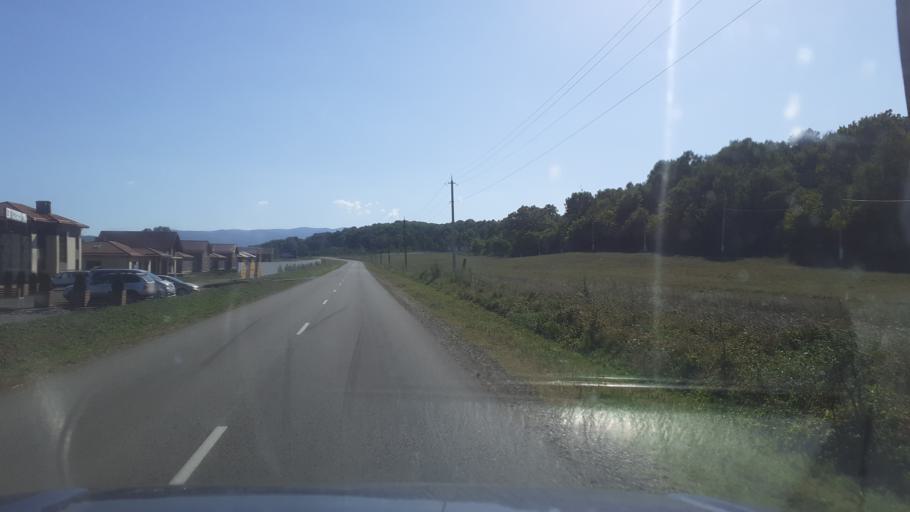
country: RU
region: Krasnodarskiy
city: Azovskaya
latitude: 44.7722
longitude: 38.5749
